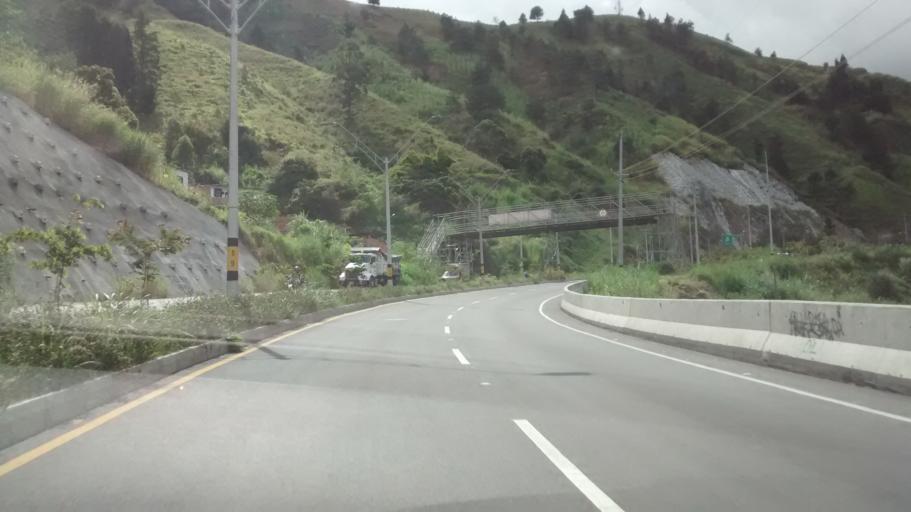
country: CO
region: Antioquia
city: Medellin
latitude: 6.2728
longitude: -75.6168
